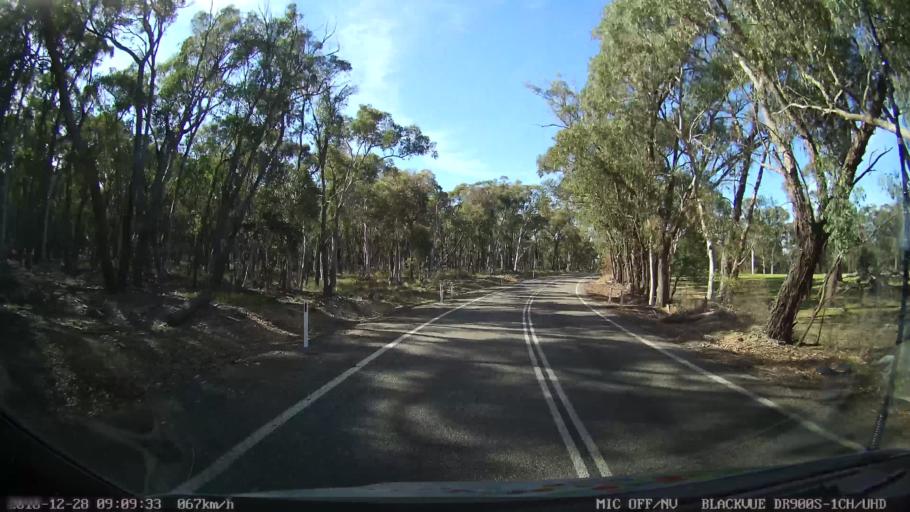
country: AU
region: New South Wales
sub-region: Upper Lachlan Shire
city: Crookwell
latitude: -34.2226
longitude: 149.3362
